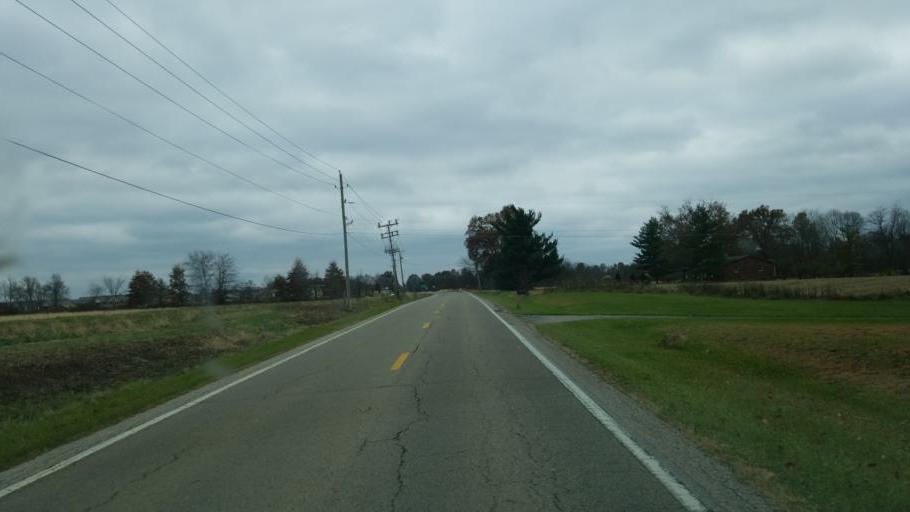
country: US
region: Ohio
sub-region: Franklin County
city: New Albany
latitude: 40.1083
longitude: -82.8380
